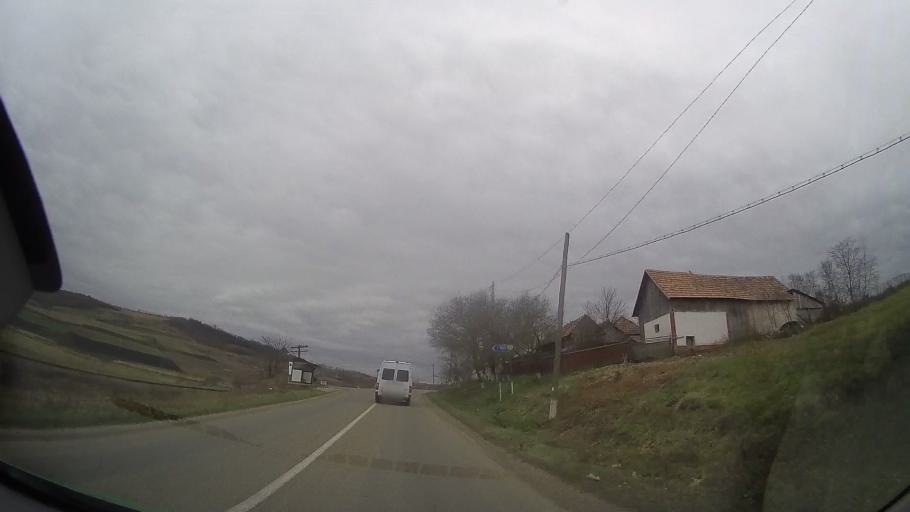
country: RO
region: Cluj
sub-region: Comuna Catina
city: Catina
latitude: 46.7976
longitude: 24.2132
